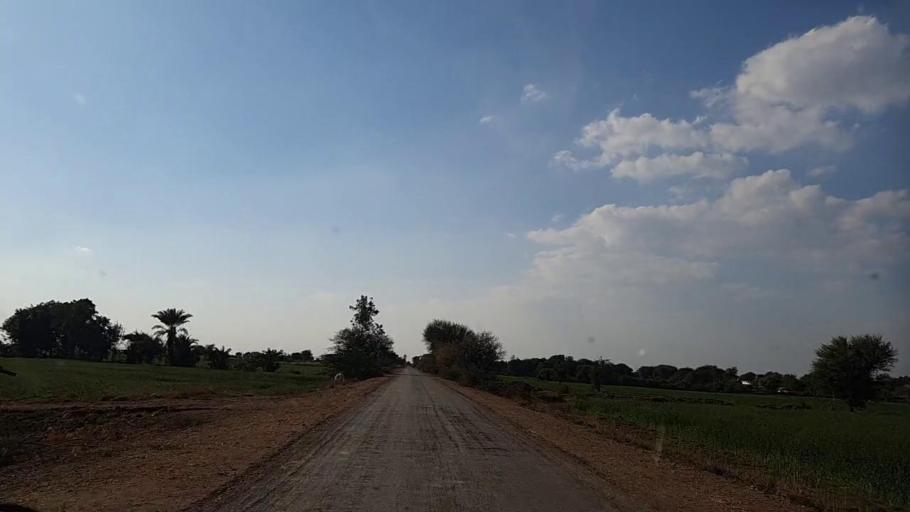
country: PK
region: Sindh
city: Pithoro
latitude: 25.6509
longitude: 69.2707
